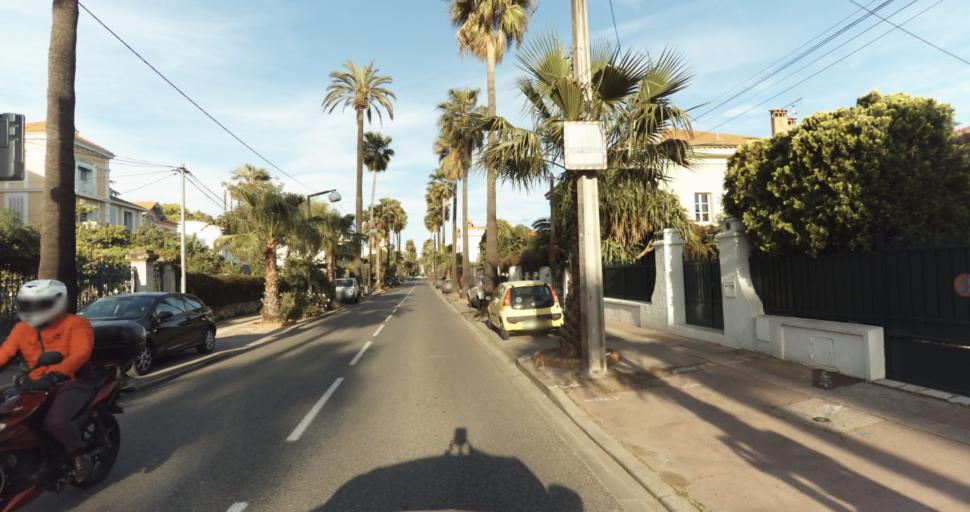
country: FR
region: Provence-Alpes-Cote d'Azur
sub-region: Departement du Var
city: Hyeres
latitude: 43.1177
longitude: 6.1245
